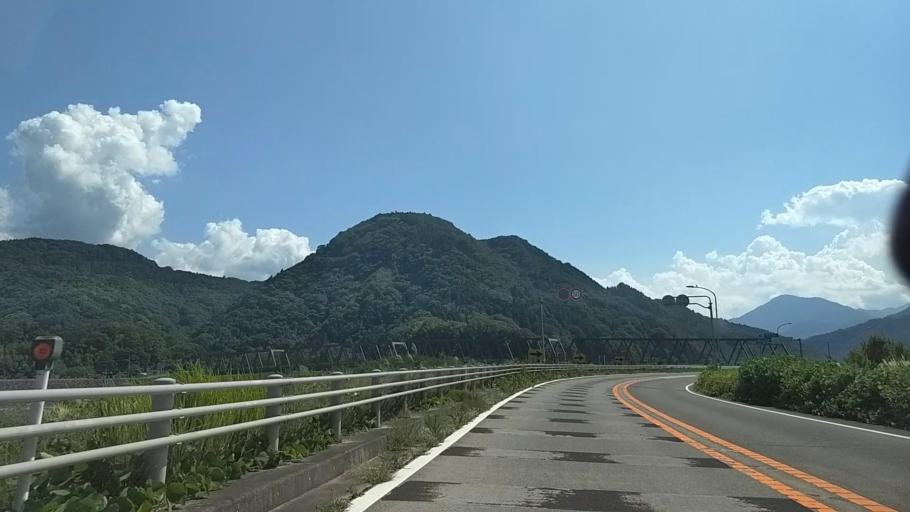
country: JP
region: Yamanashi
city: Ryuo
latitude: 35.4875
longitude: 138.4537
